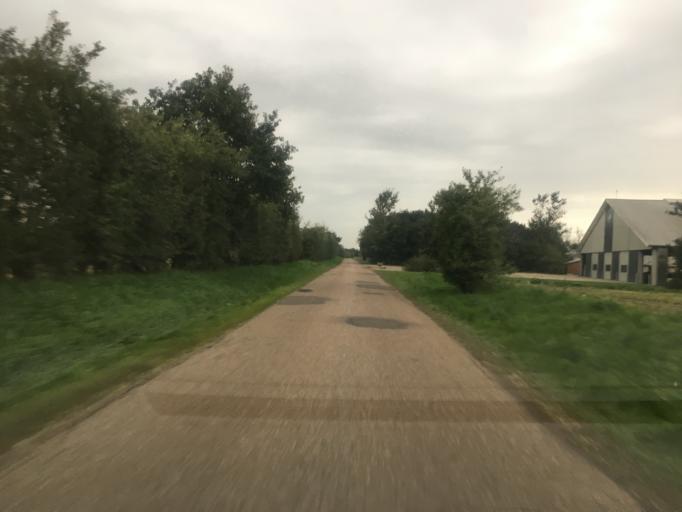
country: DE
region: Schleswig-Holstein
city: Ellhoft
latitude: 54.9538
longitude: 8.9829
